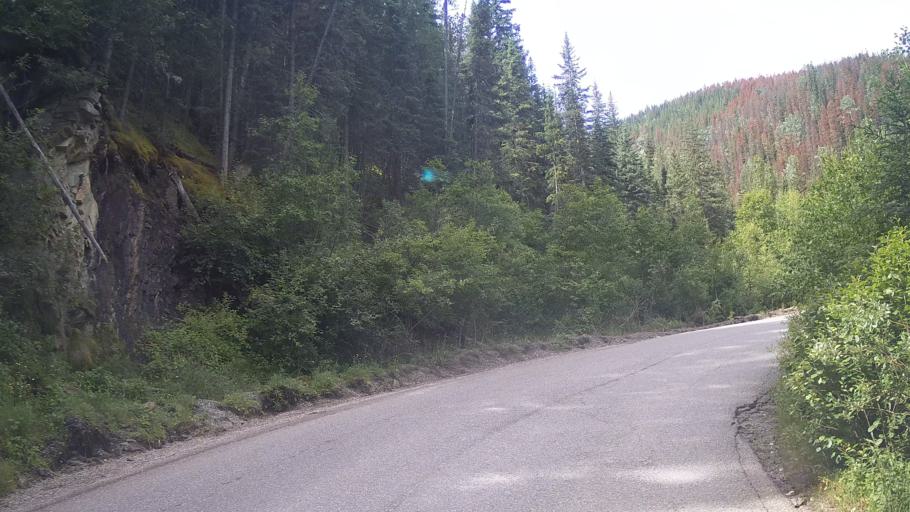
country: CA
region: Alberta
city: Hinton
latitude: 53.1757
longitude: -117.8395
